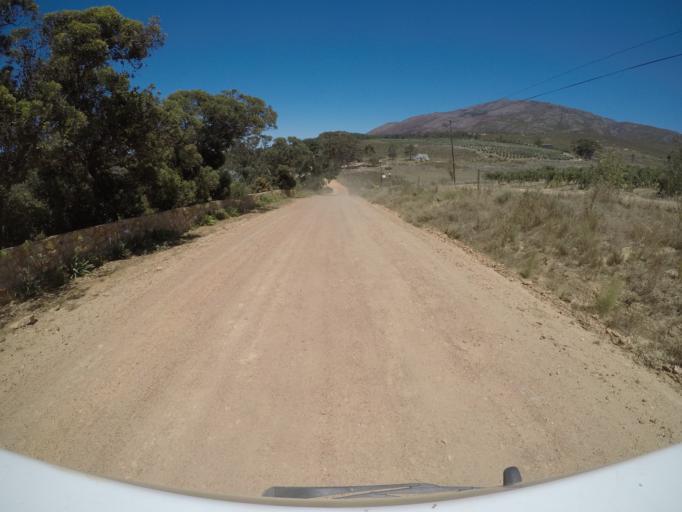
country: ZA
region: Western Cape
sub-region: Overberg District Municipality
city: Caledon
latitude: -34.1787
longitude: 19.2248
